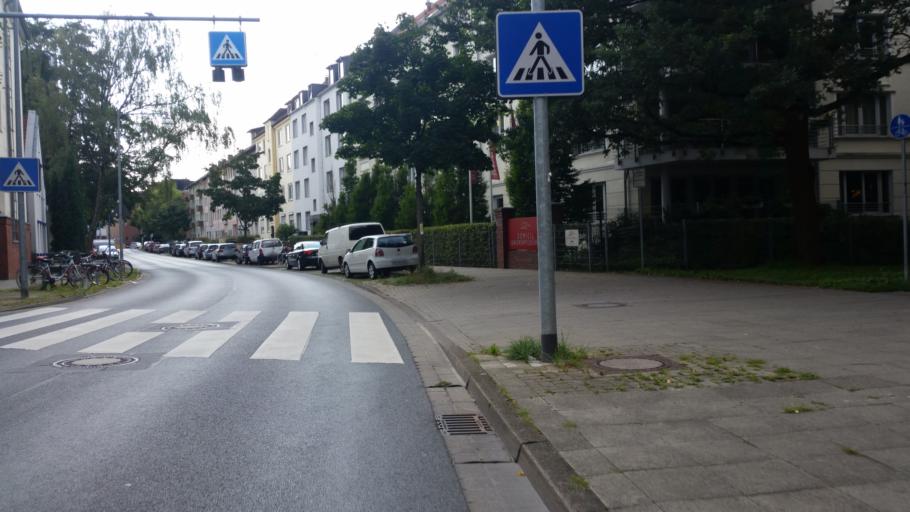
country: DE
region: Lower Saxony
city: Hannover
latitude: 52.3970
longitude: 9.7625
